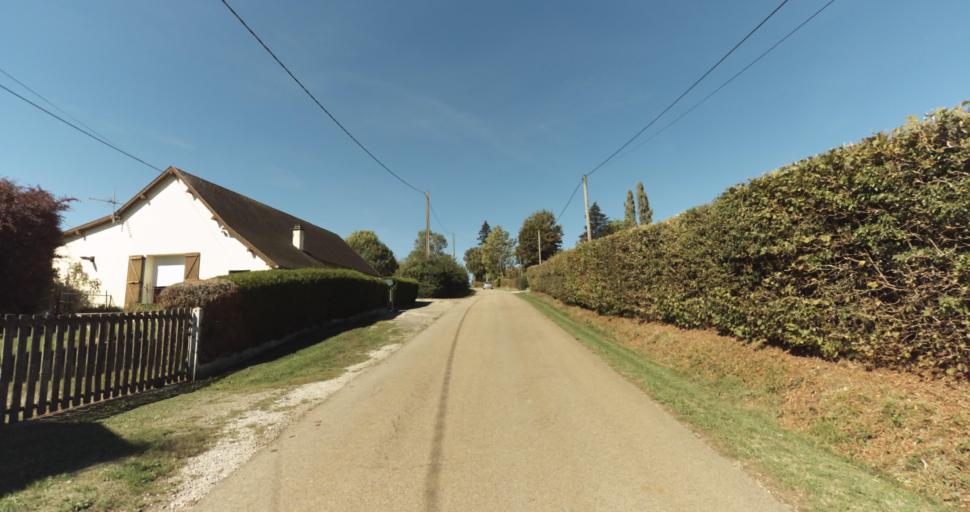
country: FR
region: Lower Normandy
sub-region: Departement de l'Orne
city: Gace
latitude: 48.7822
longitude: 0.2764
